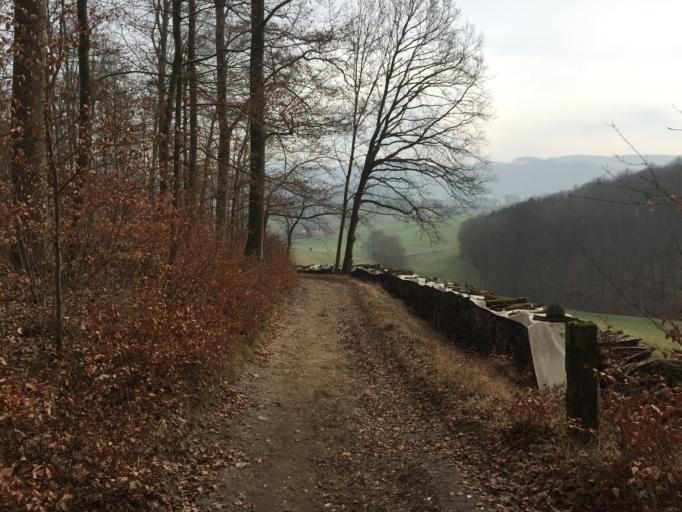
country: DE
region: Hesse
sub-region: Regierungsbezirk Darmstadt
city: Birkenau
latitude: 49.5755
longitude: 8.6941
